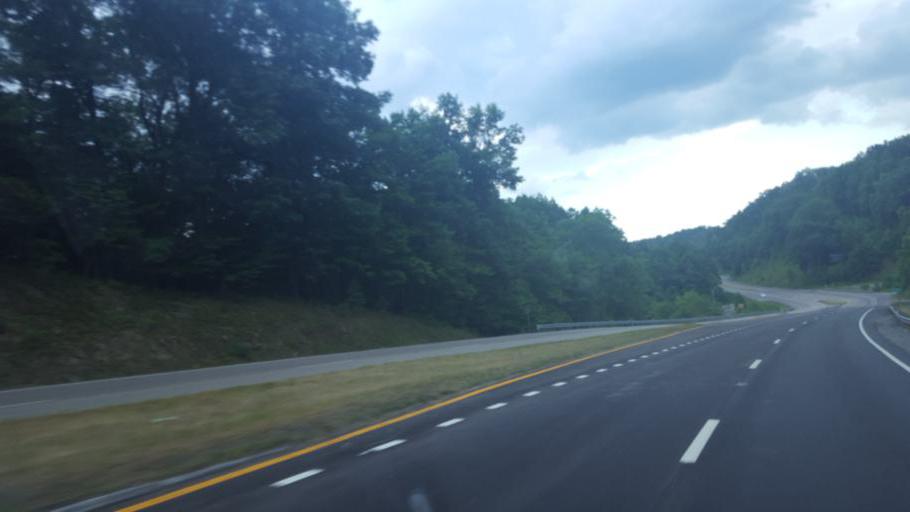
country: US
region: Virginia
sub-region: Wise County
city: Pound
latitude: 37.1441
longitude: -82.6208
